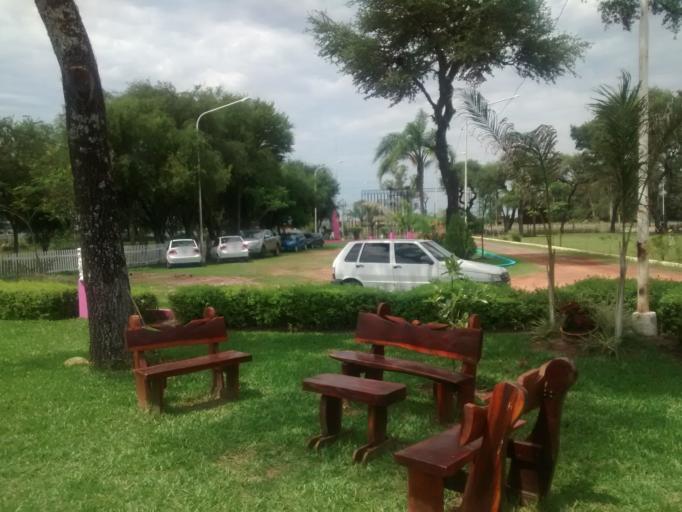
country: AR
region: Chaco
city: Fontana
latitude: -27.4022
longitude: -59.0153
